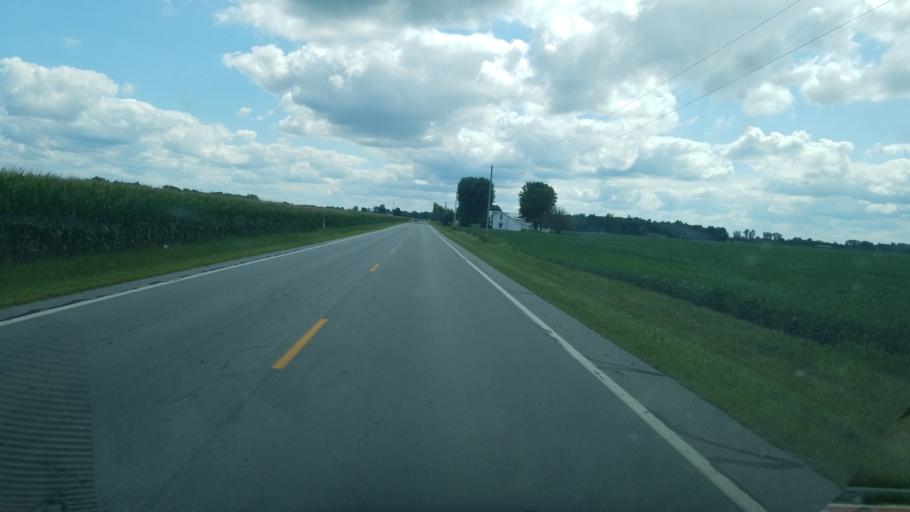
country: US
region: Ohio
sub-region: Allen County
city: Elida
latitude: 40.8398
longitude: -84.1379
